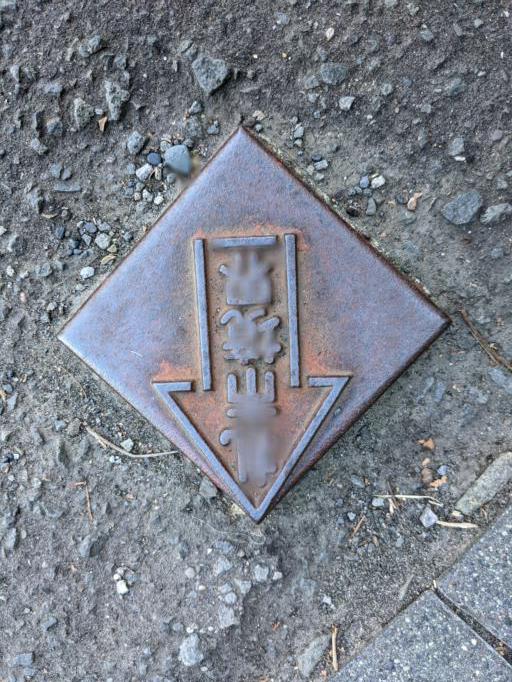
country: JP
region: Hokkaido
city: Sapporo
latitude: 43.0528
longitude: 141.2906
